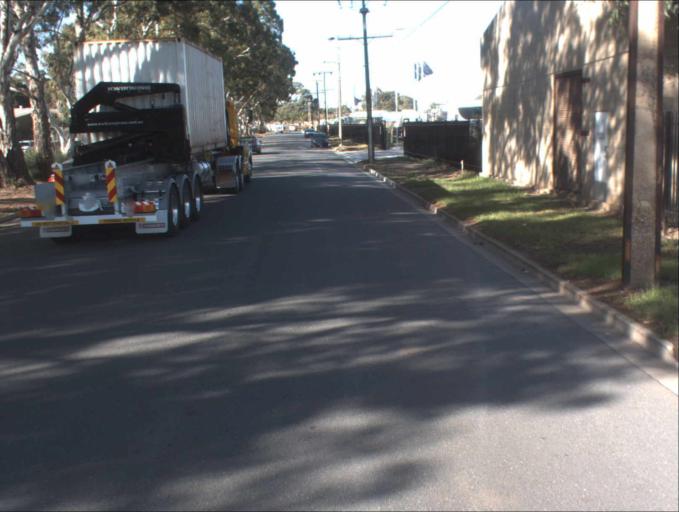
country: AU
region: South Australia
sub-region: Charles Sturt
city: Woodville North
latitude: -34.8482
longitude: 138.5542
